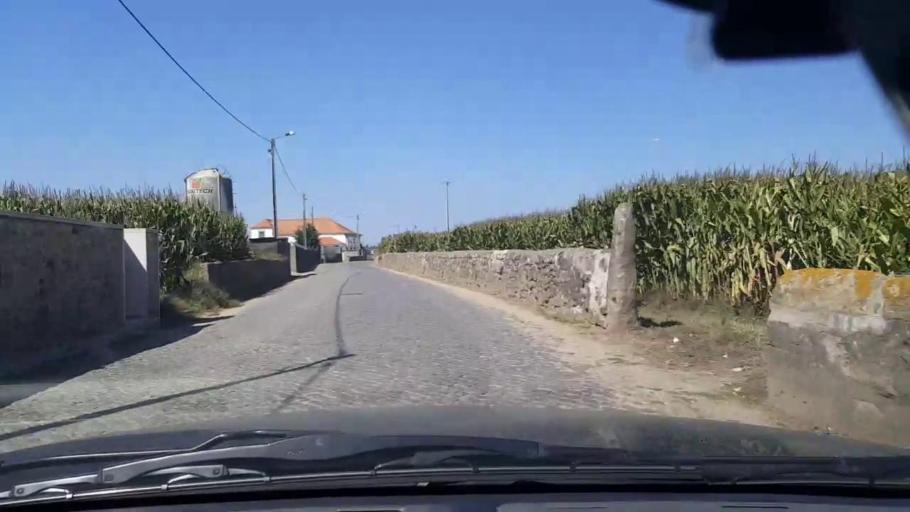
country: PT
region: Porto
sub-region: Matosinhos
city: Lavra
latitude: 41.2775
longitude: -8.7117
